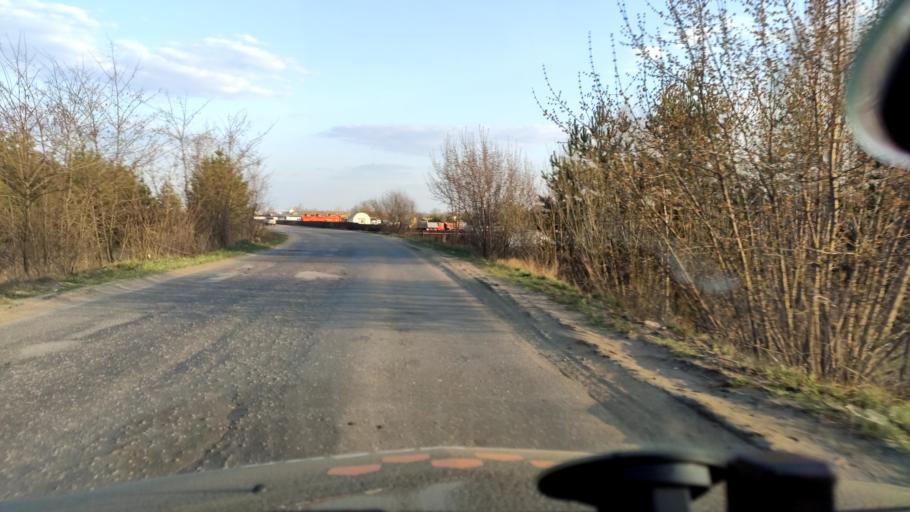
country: RU
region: Voronezj
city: Podgornoye
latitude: 51.8289
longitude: 39.2073
